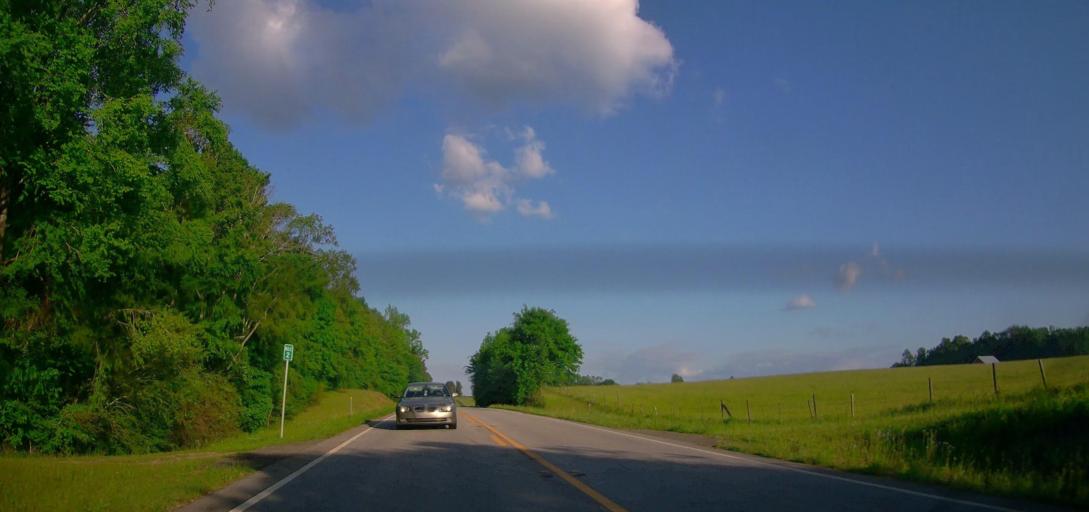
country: US
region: Georgia
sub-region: Jasper County
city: Monticello
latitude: 33.3890
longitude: -83.5669
